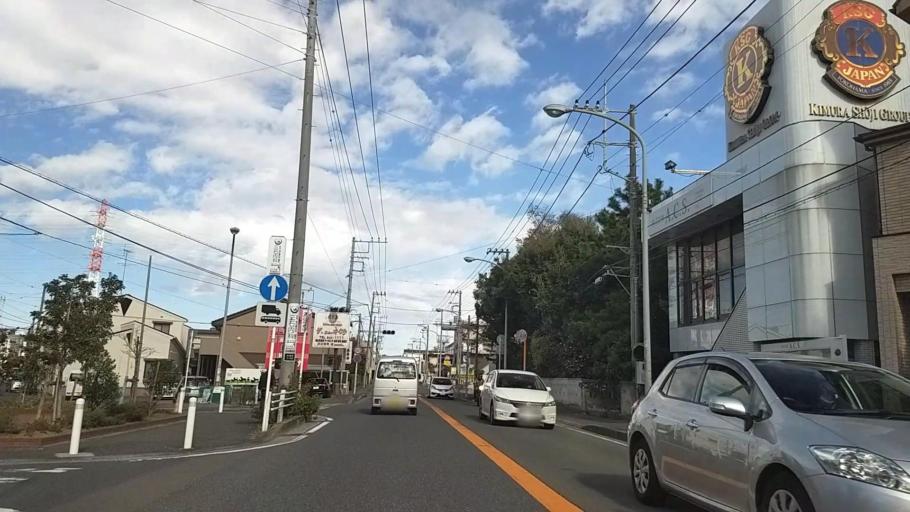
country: JP
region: Kanagawa
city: Yokohama
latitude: 35.5270
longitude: 139.6331
